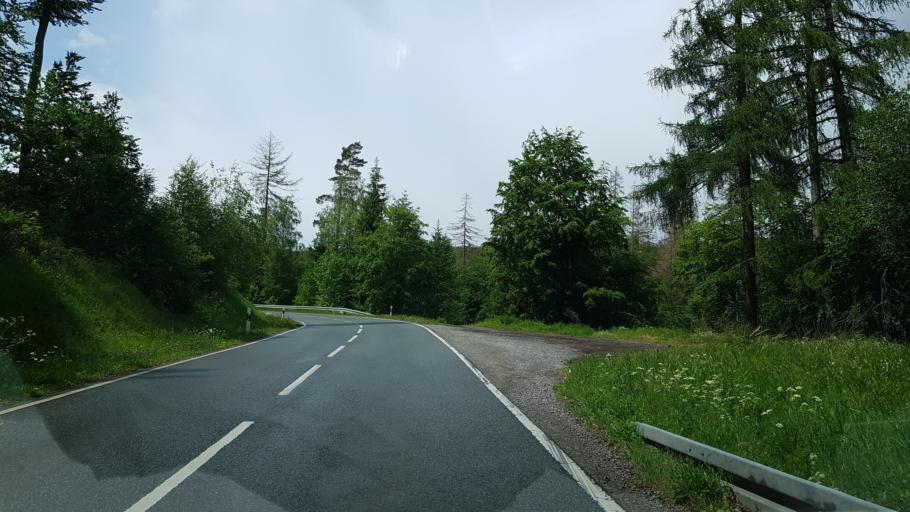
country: DE
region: Lower Saxony
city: Bodenfelde
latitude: 51.5988
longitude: 9.5253
